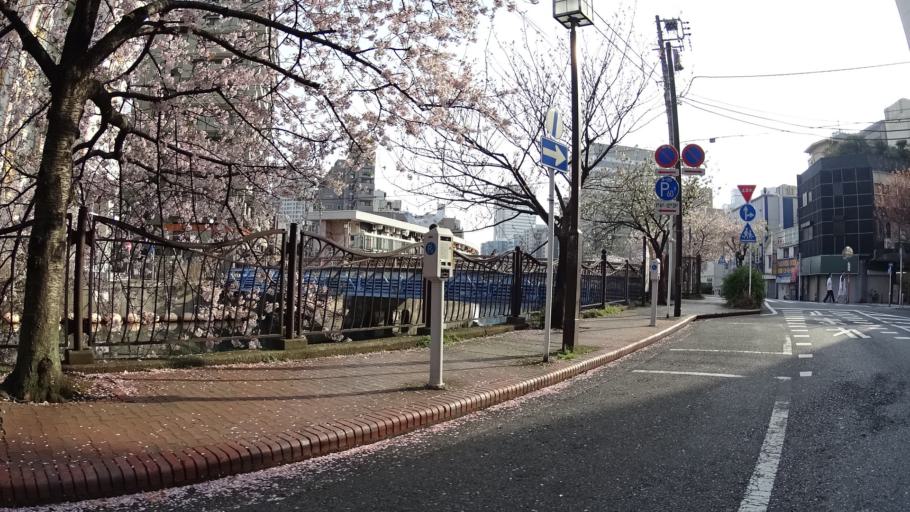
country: JP
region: Kanagawa
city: Yokohama
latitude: 35.4459
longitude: 139.6299
